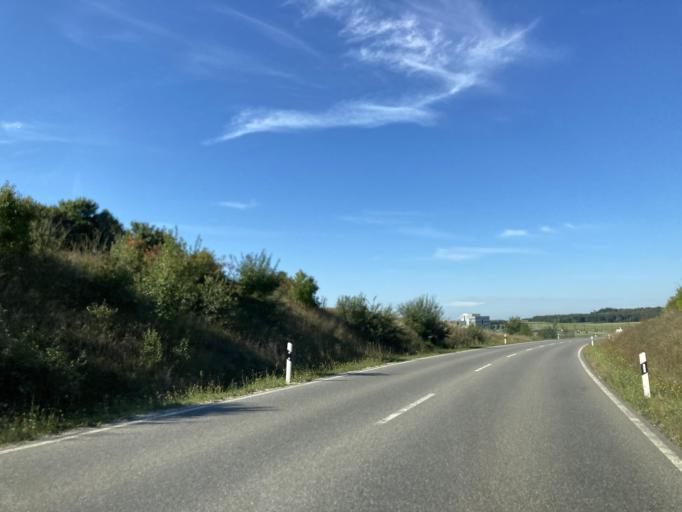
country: DE
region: Baden-Wuerttemberg
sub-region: Tuebingen Region
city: Biberach an der Riss
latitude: 48.1121
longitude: 9.7743
